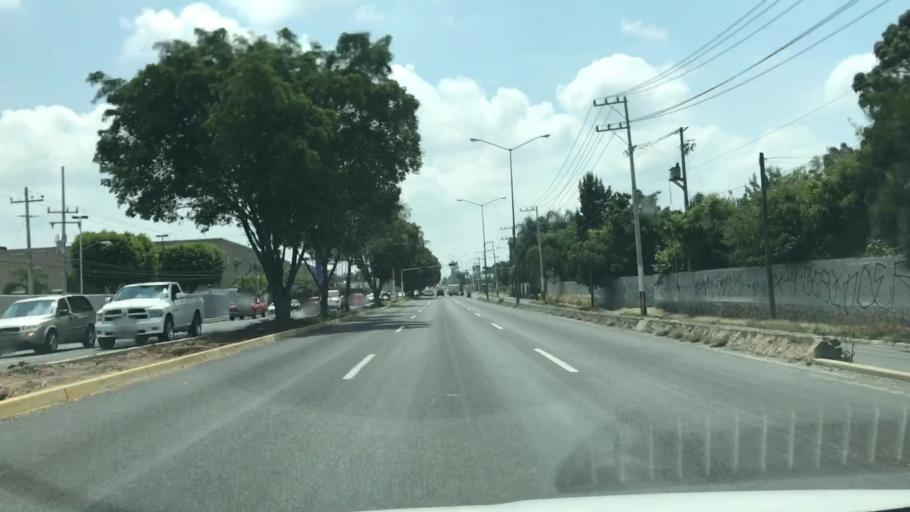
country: MX
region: Jalisco
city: Nuevo Mexico
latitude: 20.7573
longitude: -103.4297
